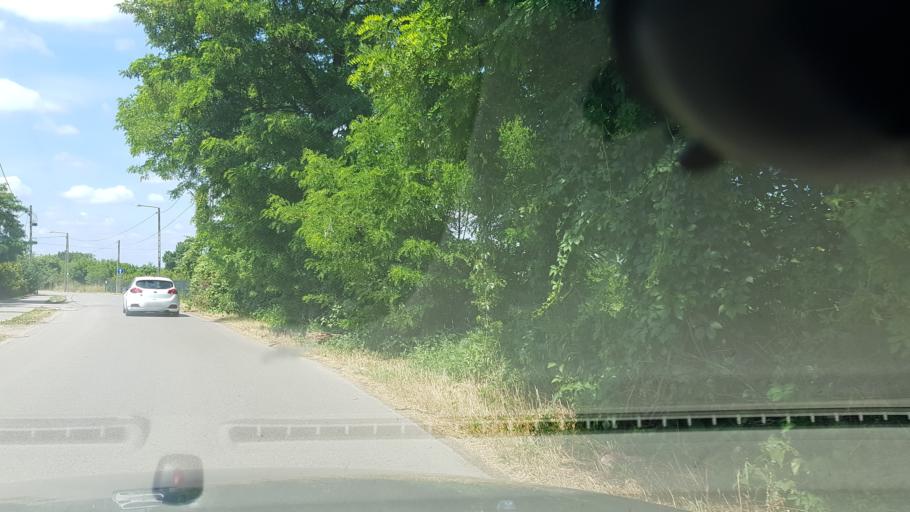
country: PL
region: Masovian Voivodeship
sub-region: Warszawa
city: Targowek
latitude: 52.3049
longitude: 21.0400
